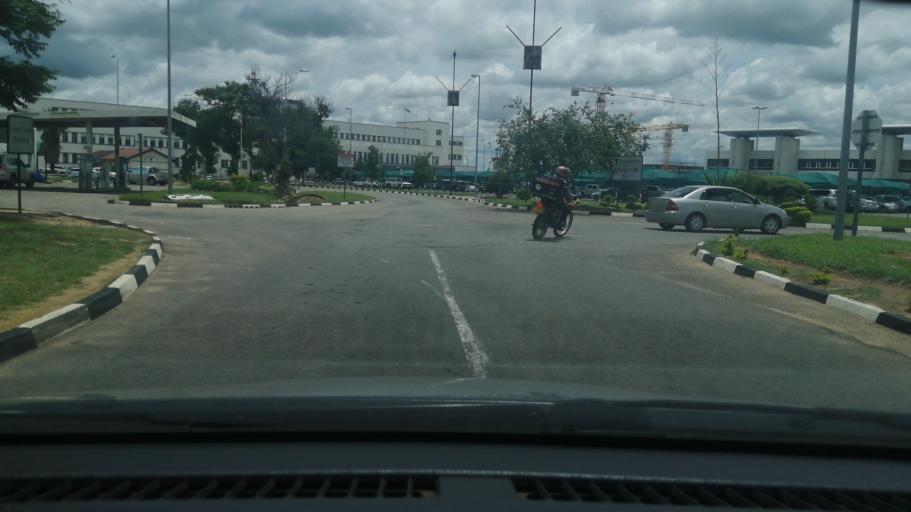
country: ZW
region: Harare
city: Epworth
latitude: -17.9173
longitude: 31.0998
